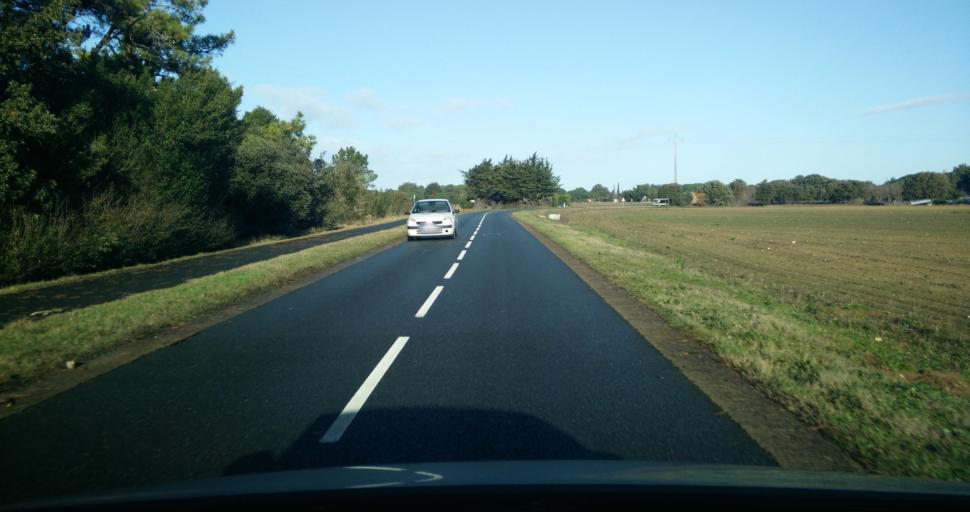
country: FR
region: Poitou-Charentes
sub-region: Departement de la Charente-Maritime
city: La Flotte
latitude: 46.1752
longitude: -1.3306
